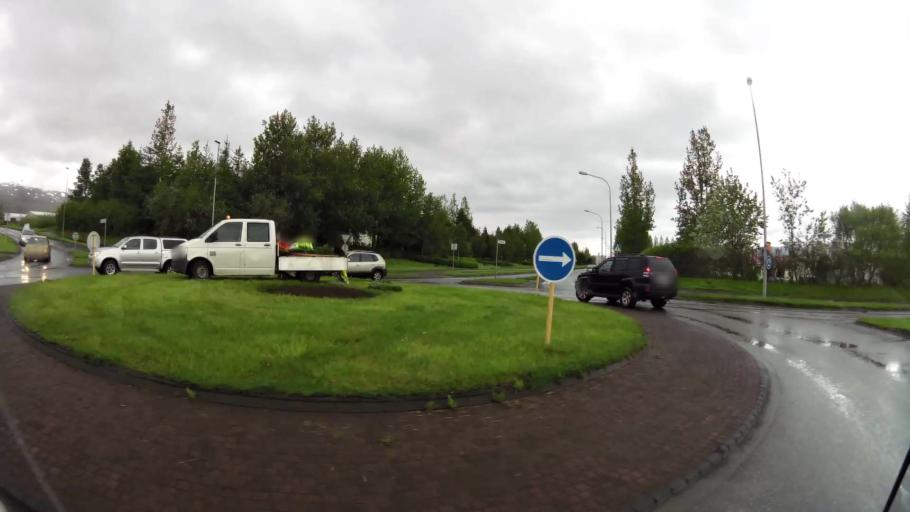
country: IS
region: Northeast
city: Akureyri
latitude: 65.6872
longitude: -18.1290
